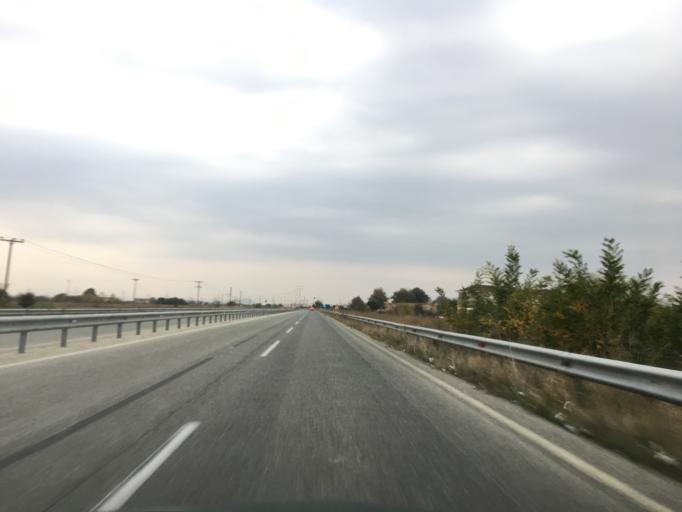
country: GR
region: Thessaly
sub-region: Trikala
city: Megalochori
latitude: 39.5641
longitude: 21.8519
